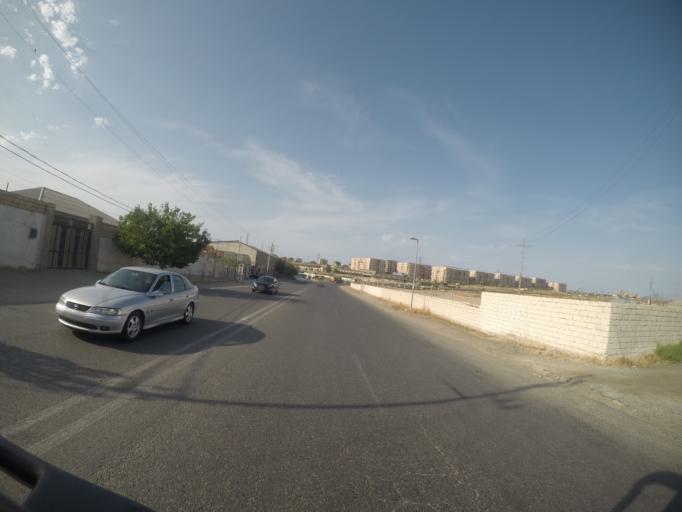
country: AZ
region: Baki
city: Binagadi
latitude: 40.4789
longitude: 49.8343
